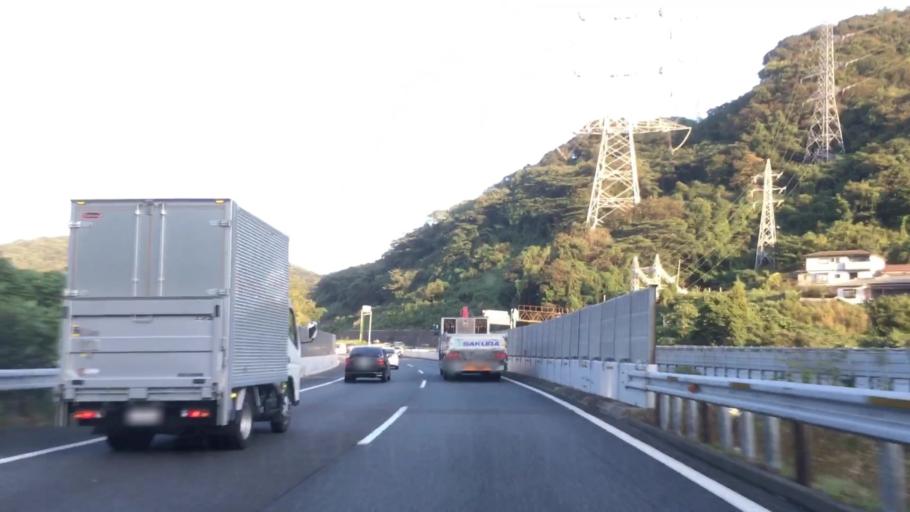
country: JP
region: Yamaguchi
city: Shimonoseki
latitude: 33.9519
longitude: 130.9839
